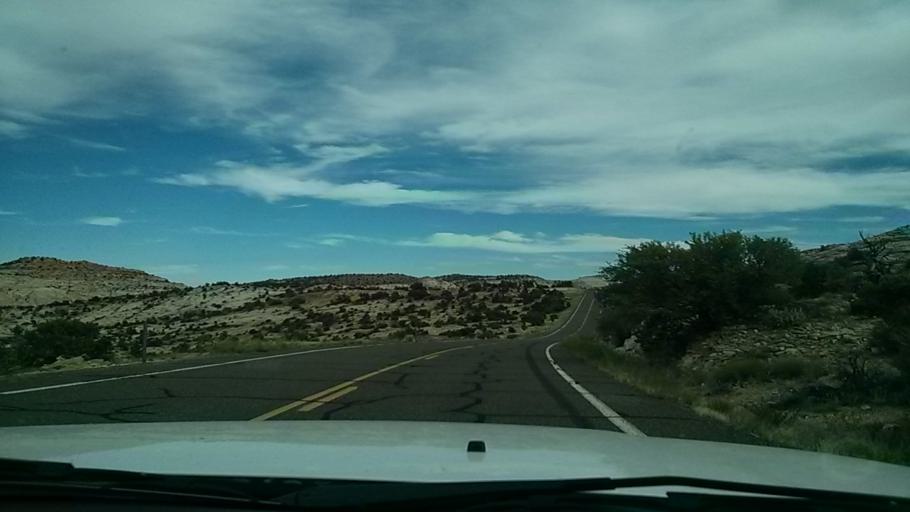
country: US
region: Utah
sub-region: Wayne County
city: Loa
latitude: 37.8100
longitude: -111.4045
